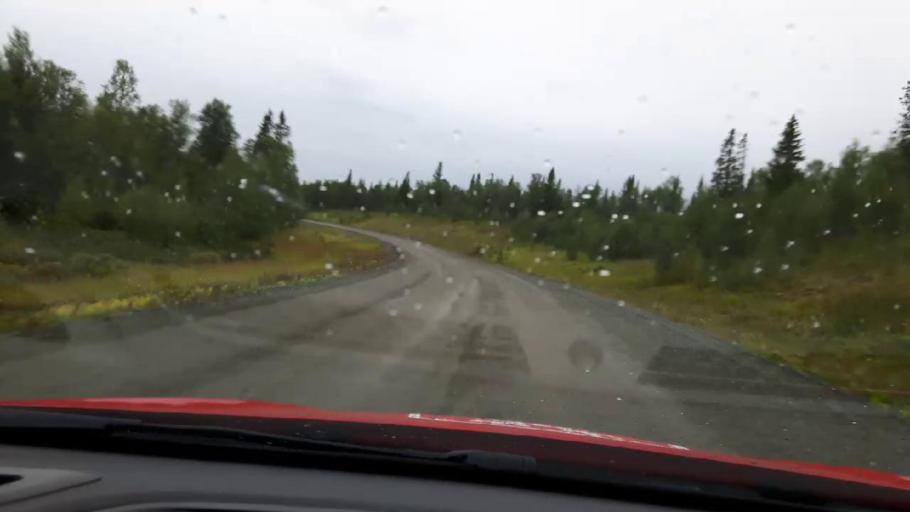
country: NO
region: Nord-Trondelag
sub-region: Meraker
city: Meraker
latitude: 63.5651
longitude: 12.2873
